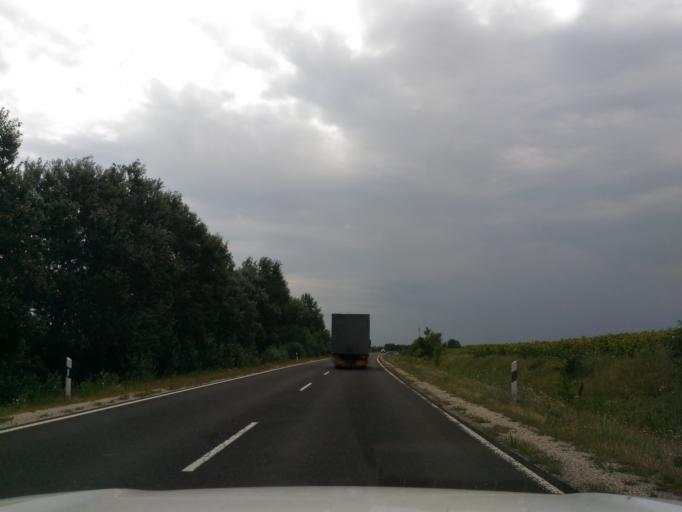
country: HU
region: Pest
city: Abony
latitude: 47.1916
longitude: 20.0901
